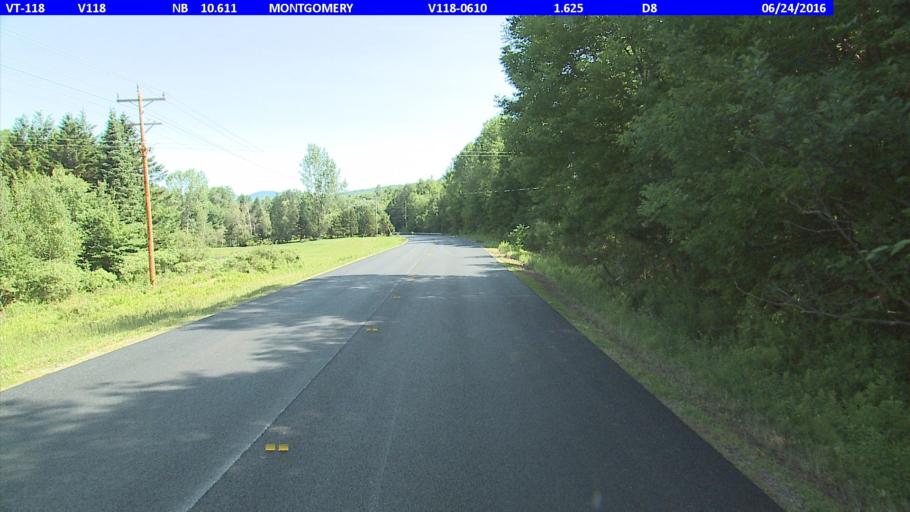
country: US
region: Vermont
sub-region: Franklin County
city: Richford
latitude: 44.8216
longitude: -72.6112
